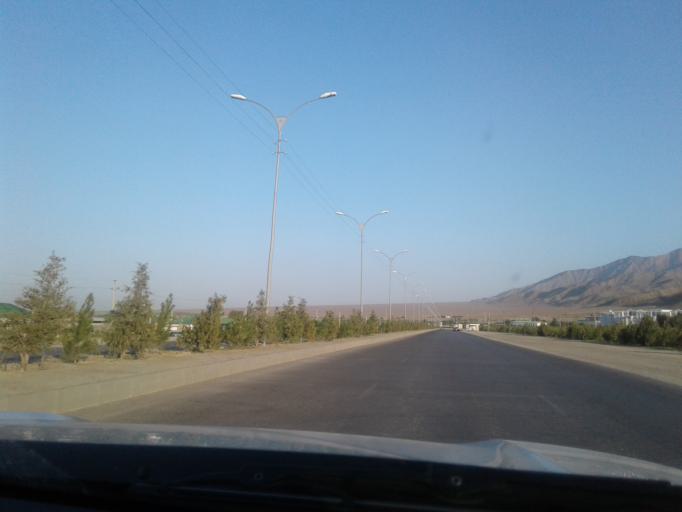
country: TM
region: Ahal
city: Baharly
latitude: 38.5236
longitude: 57.1788
